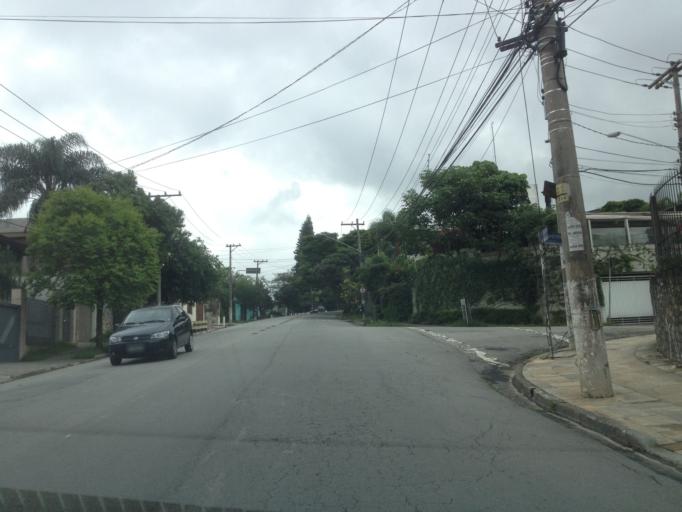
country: BR
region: Sao Paulo
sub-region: Sao Paulo
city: Sao Paulo
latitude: -23.5452
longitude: -46.6986
